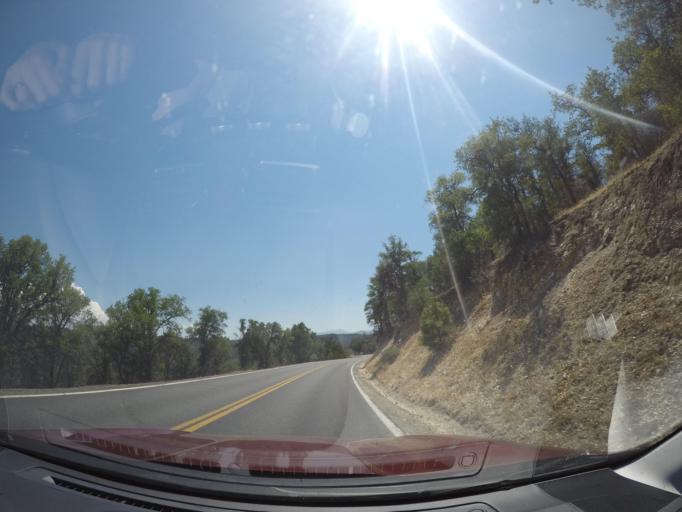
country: US
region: California
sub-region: Shasta County
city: Burney
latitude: 40.9941
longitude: -121.5116
